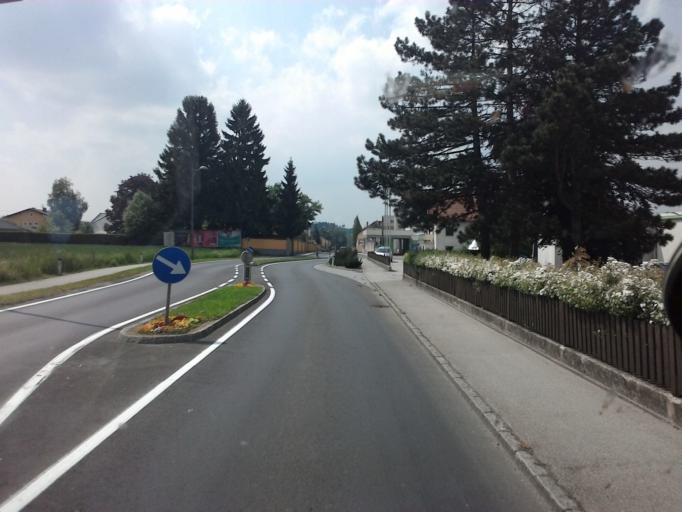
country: AT
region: Upper Austria
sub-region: Wels-Land
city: Sattledt
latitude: 48.0728
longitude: 14.0629
